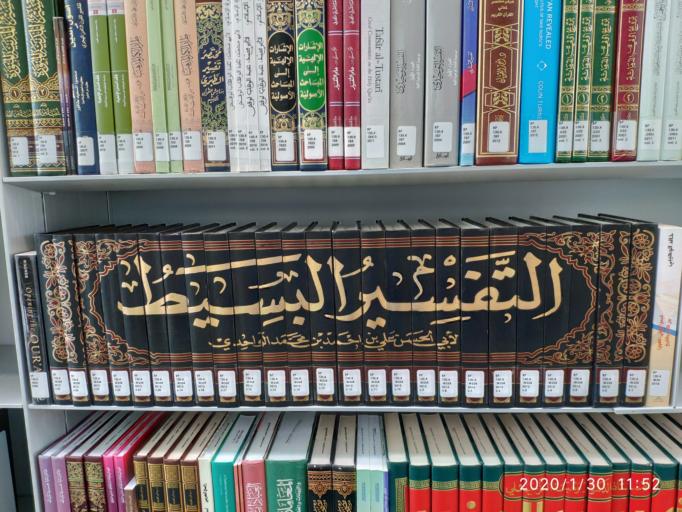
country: QA
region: Baladiyat ar Rayyan
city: Ar Rayyan
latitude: 25.3178
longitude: 51.4416
